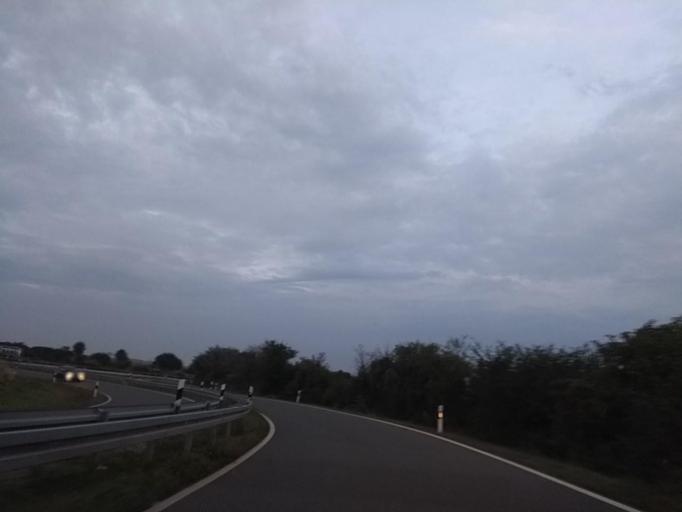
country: DE
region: Saxony-Anhalt
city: Lutzen
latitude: 51.2396
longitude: 12.1362
